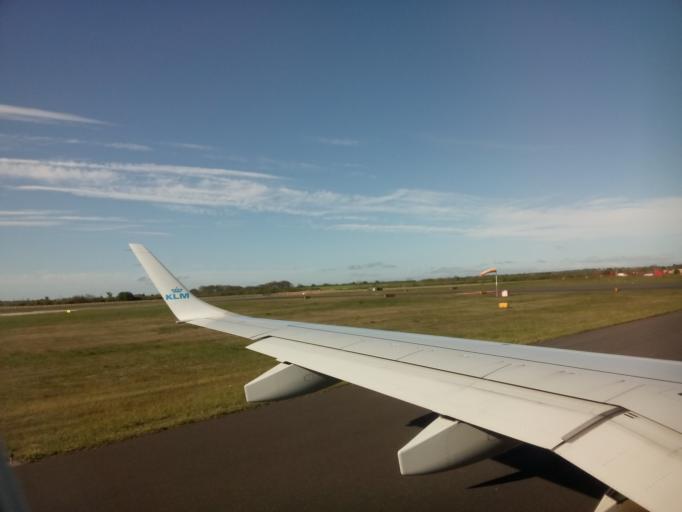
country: GB
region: England
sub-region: Newcastle upon Tyne
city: Dinnington
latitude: 55.0360
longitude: -1.7038
